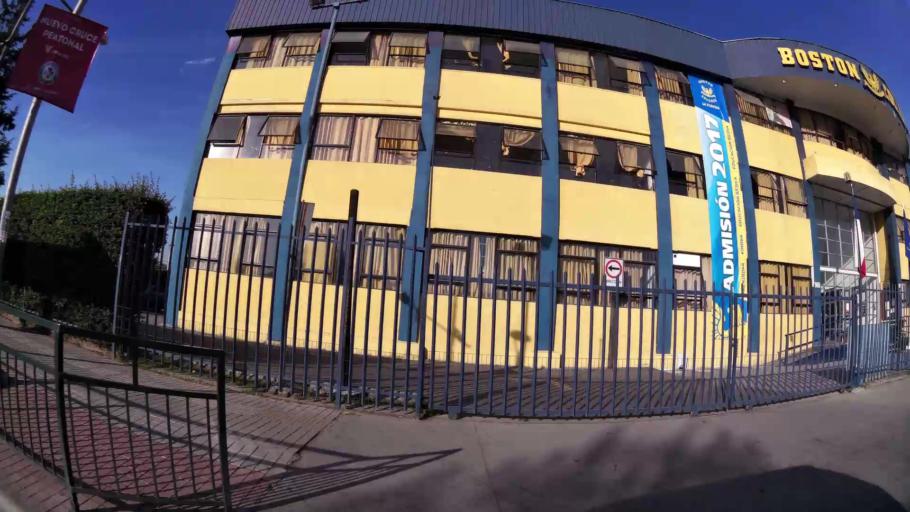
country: CL
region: Santiago Metropolitan
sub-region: Provincia de Cordillera
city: Puente Alto
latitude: -33.5440
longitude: -70.5696
